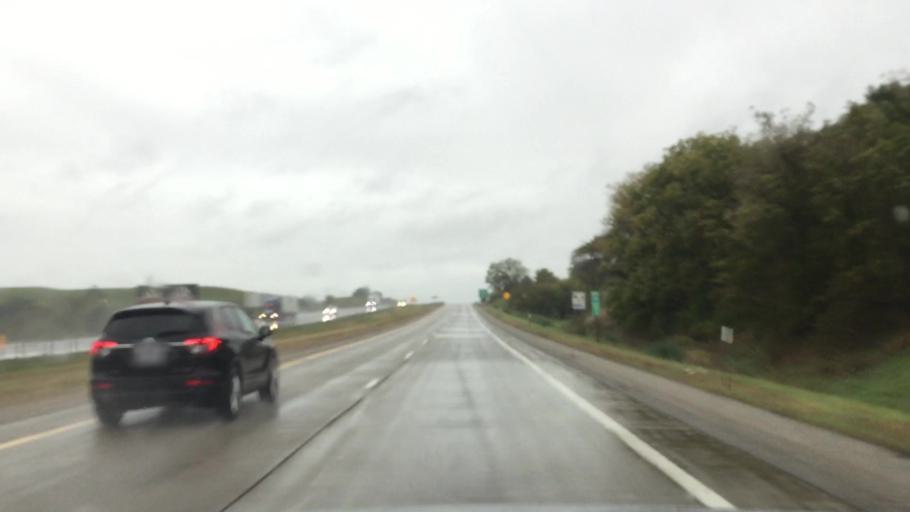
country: US
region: Michigan
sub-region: Berrien County
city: Watervliet
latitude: 42.1776
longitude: -86.2765
